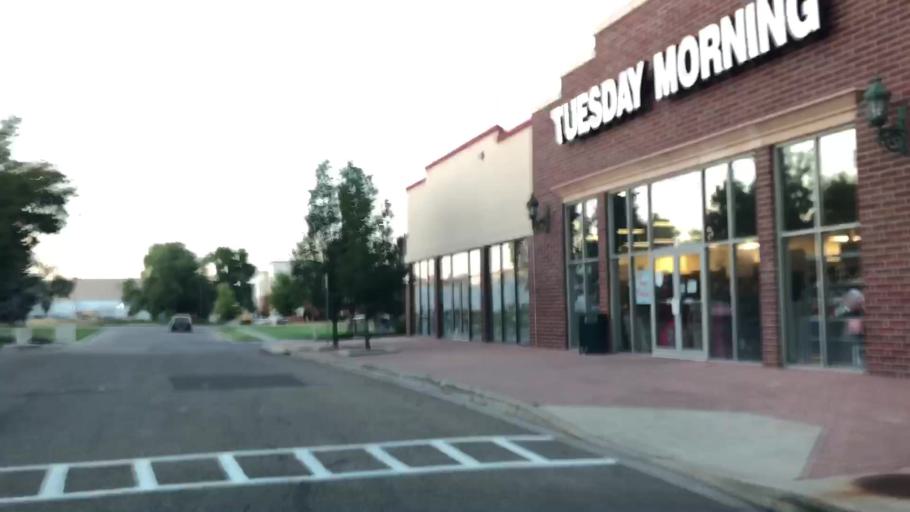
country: US
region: Colorado
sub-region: Larimer County
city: Fort Collins
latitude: 40.5251
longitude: -105.0745
